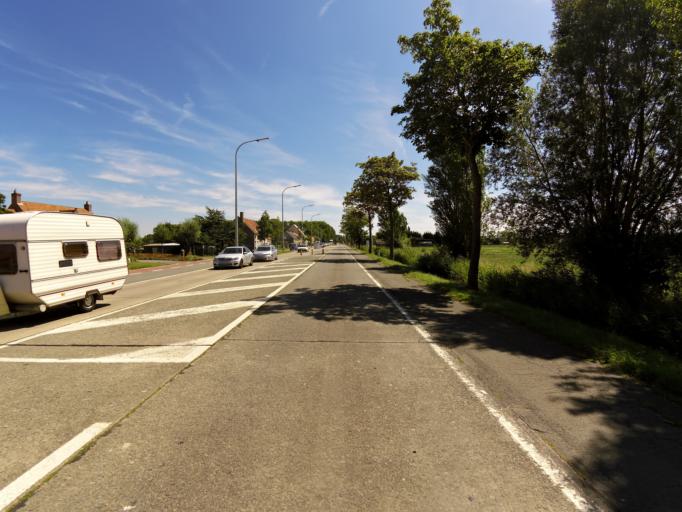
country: BE
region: Flanders
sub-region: Provincie West-Vlaanderen
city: Zuienkerke
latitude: 51.2854
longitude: 3.1642
